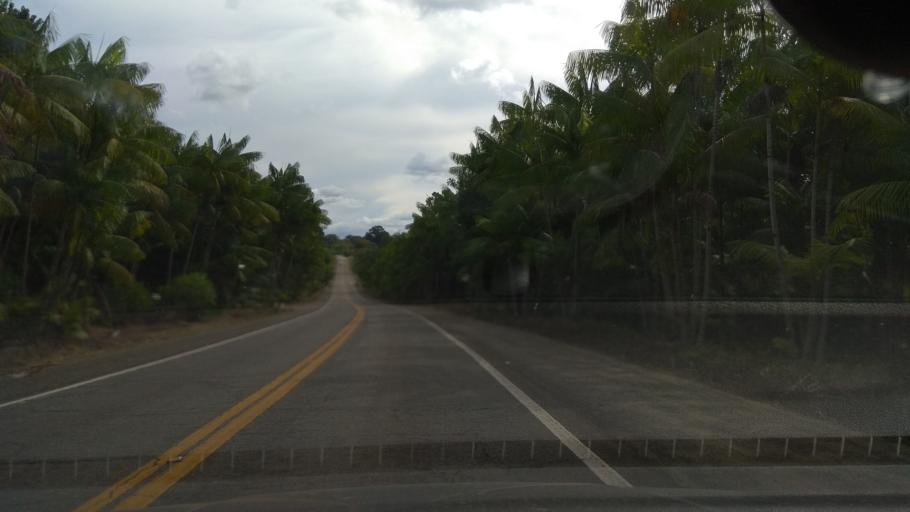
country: BR
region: Bahia
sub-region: Ubata
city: Ubata
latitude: -14.2293
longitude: -39.4385
